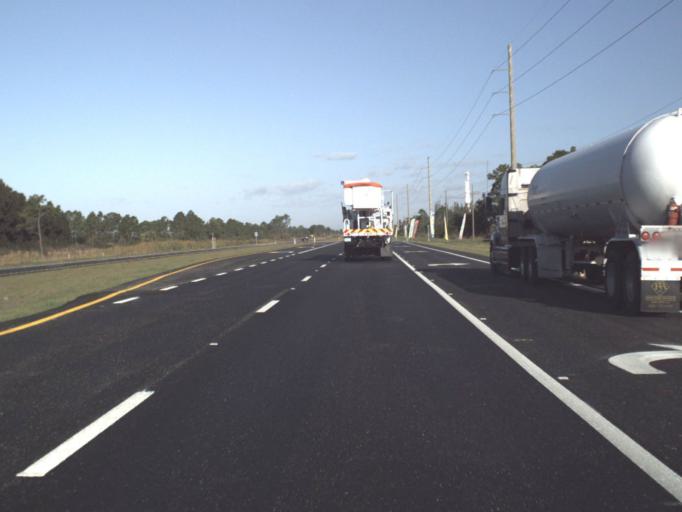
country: US
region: Florida
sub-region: Palm Beach County
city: Limestone Creek
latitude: 26.9137
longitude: -80.3074
